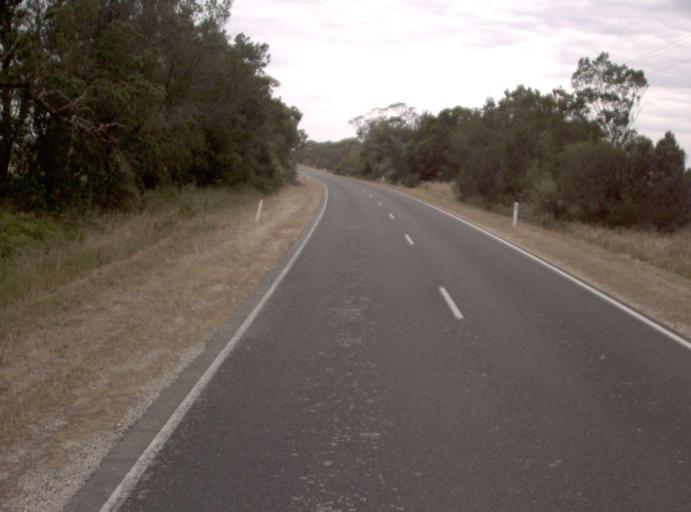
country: AU
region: Victoria
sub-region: Wellington
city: Sale
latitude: -38.2006
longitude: 147.3308
